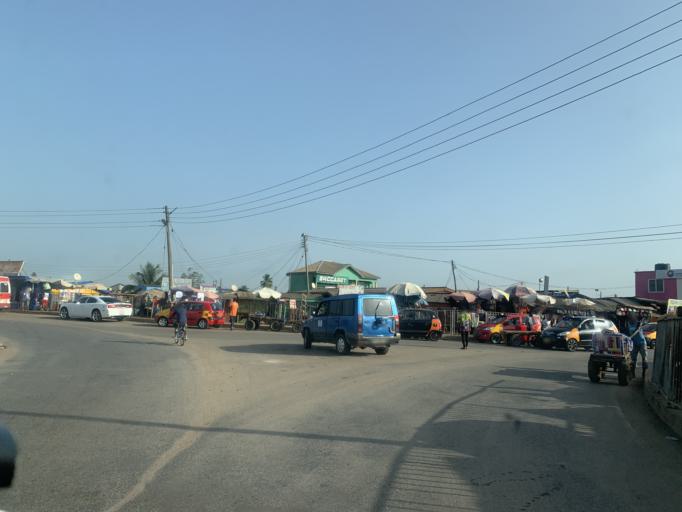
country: GH
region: Central
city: Saltpond
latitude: 5.2678
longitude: -1.0183
